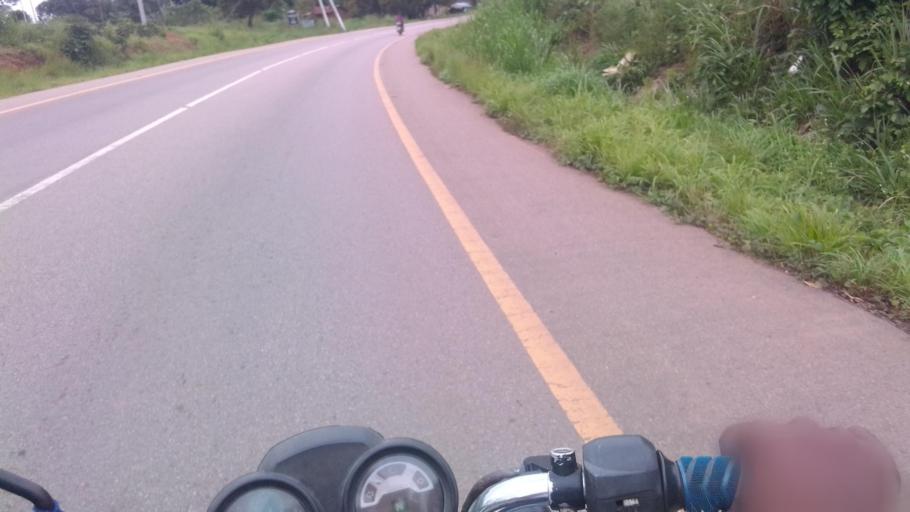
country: SL
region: Eastern Province
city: Hangha
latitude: 7.9355
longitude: -11.1470
